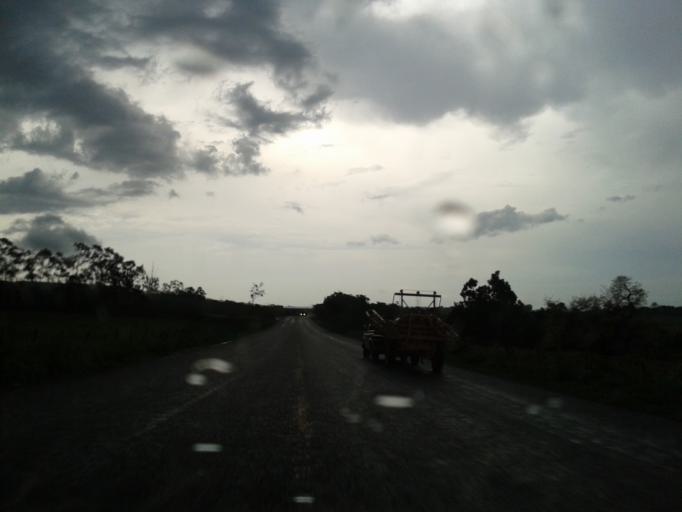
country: BR
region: Goias
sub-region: Quirinopolis
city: Quirinopolis
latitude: -18.4303
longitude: -50.4203
